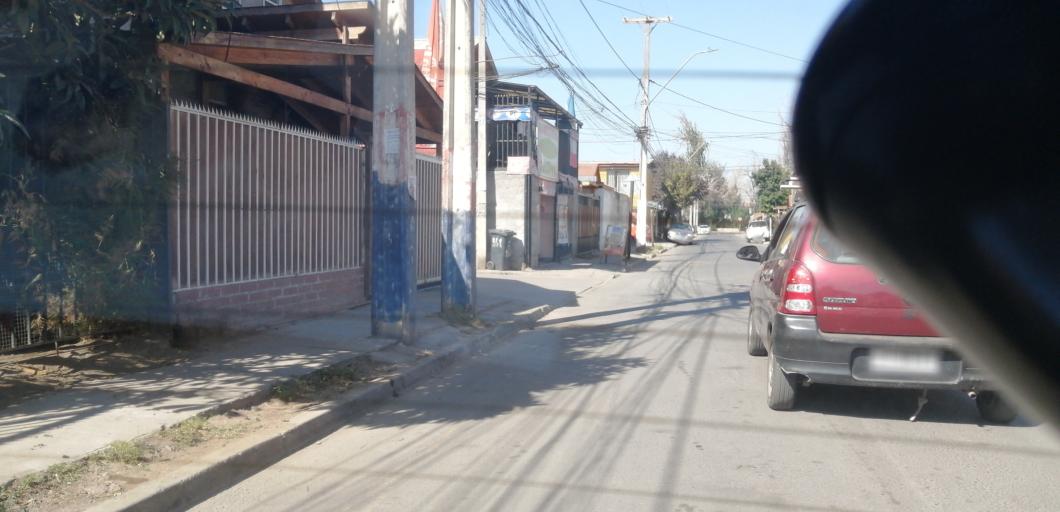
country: CL
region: Santiago Metropolitan
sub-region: Provincia de Santiago
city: Lo Prado
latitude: -33.4654
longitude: -70.7458
